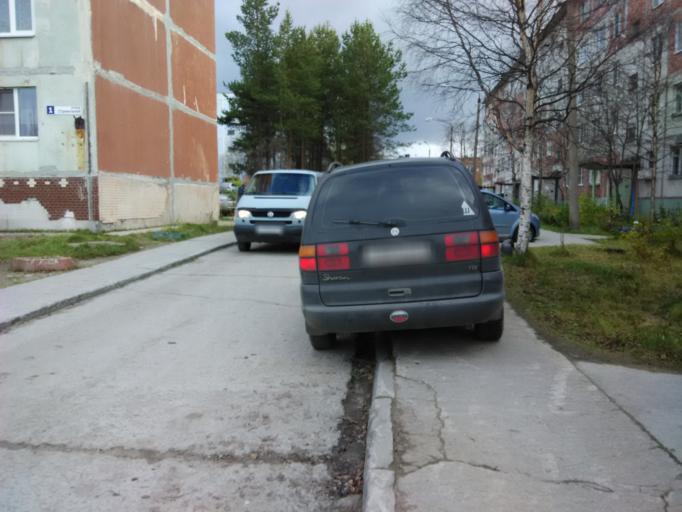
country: RU
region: Murmansk
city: Polyarnyye Zori
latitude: 67.3699
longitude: 32.4884
